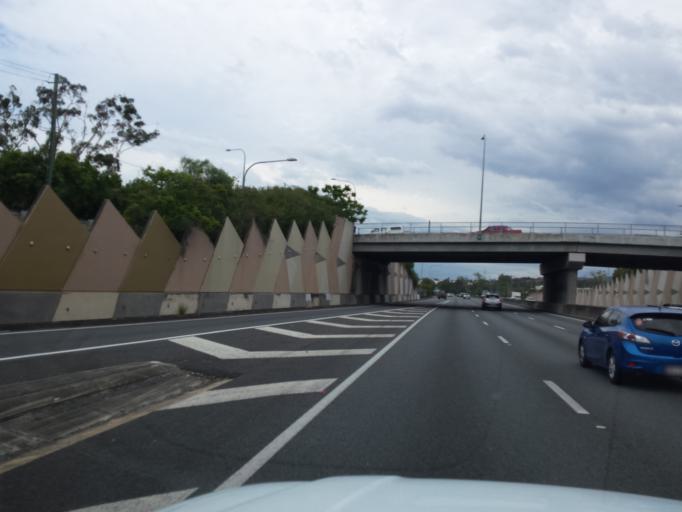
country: AU
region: Queensland
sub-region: Gold Coast
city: Nerang
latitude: -27.9960
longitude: 153.3401
